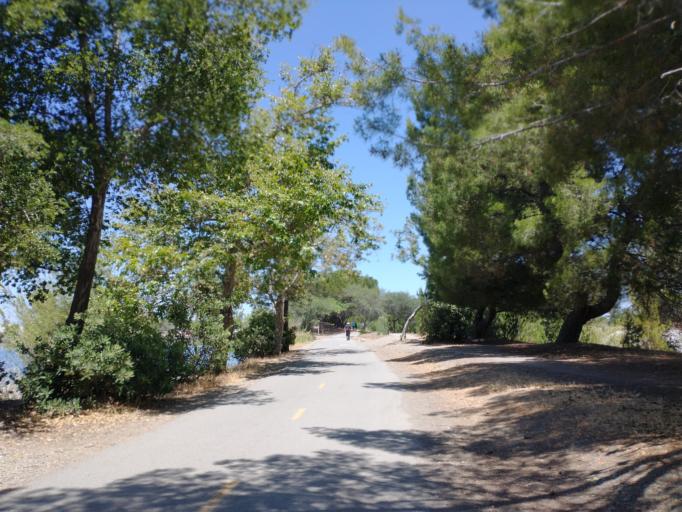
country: US
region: California
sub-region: Santa Clara County
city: Campbell
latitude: 37.2666
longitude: -121.9499
